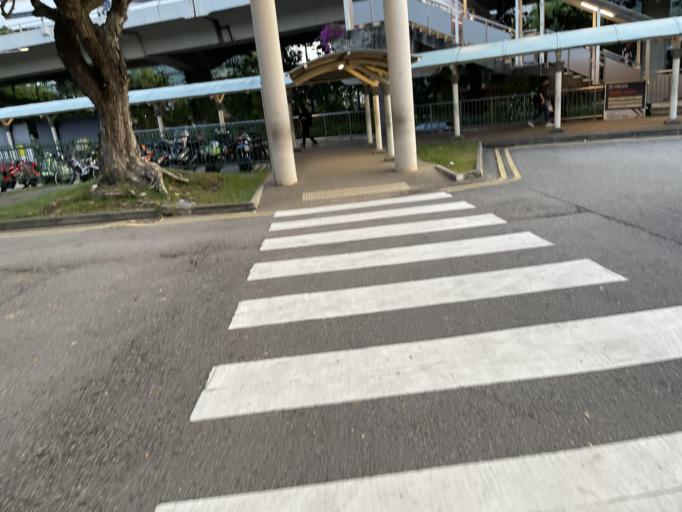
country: SG
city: Singapore
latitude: 1.2663
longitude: 103.8198
